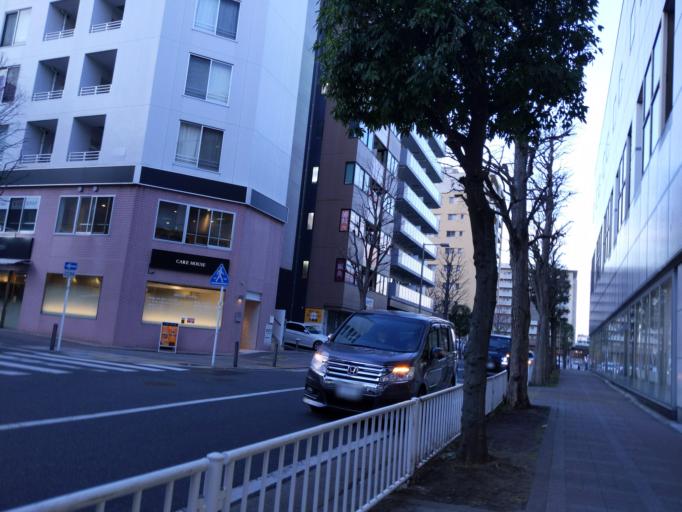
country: JP
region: Tokyo
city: Chofugaoka
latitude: 35.5455
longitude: 139.5742
